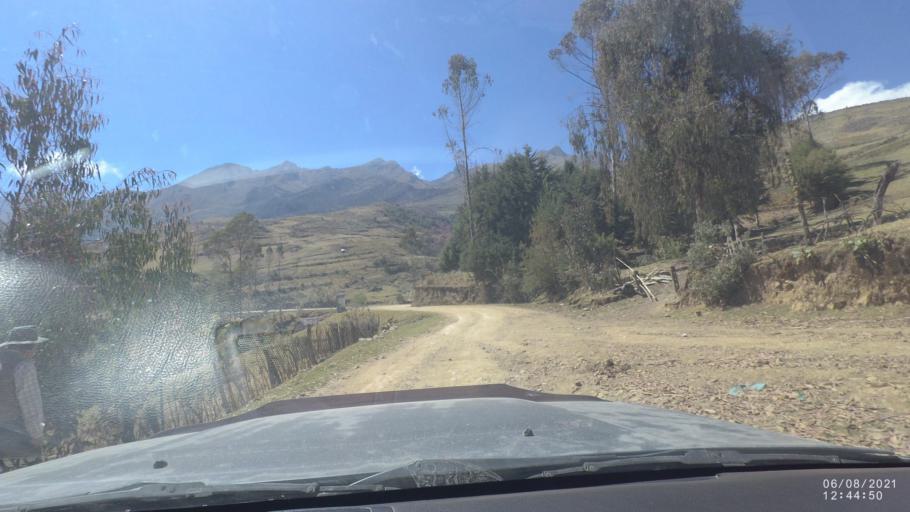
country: BO
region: Cochabamba
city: Colchani
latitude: -16.7672
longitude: -66.6647
